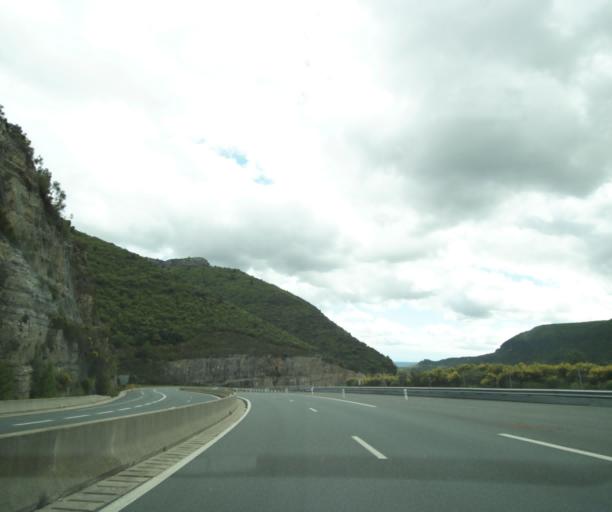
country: FR
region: Languedoc-Roussillon
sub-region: Departement de l'Herault
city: Lodeve
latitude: 43.8074
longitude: 3.3257
